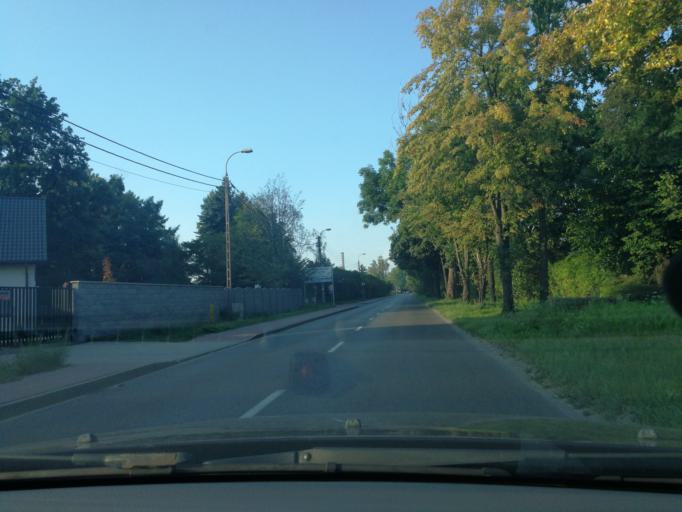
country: PL
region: Masovian Voivodeship
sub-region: Powiat pruszkowski
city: Brwinow
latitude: 52.1503
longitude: 20.7268
